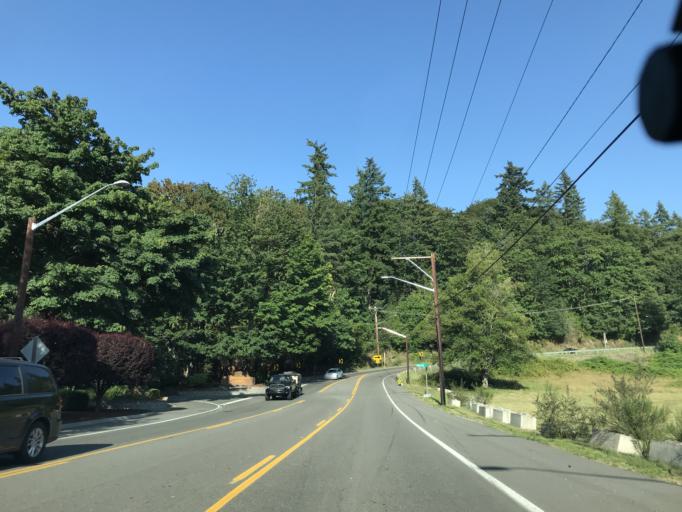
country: US
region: Washington
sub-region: King County
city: Lake Morton-Berrydale
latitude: 47.3436
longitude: -122.1015
